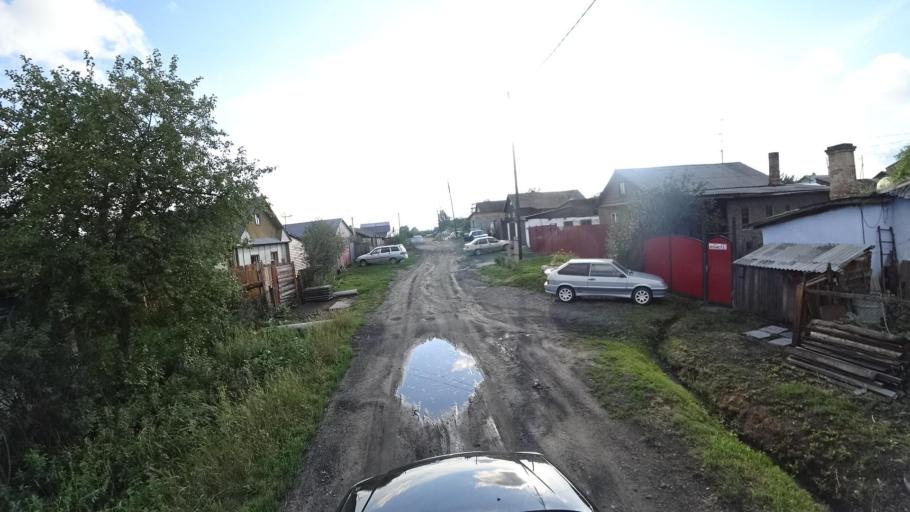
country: RU
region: Sverdlovsk
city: Kamyshlov
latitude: 56.8483
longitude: 62.6688
